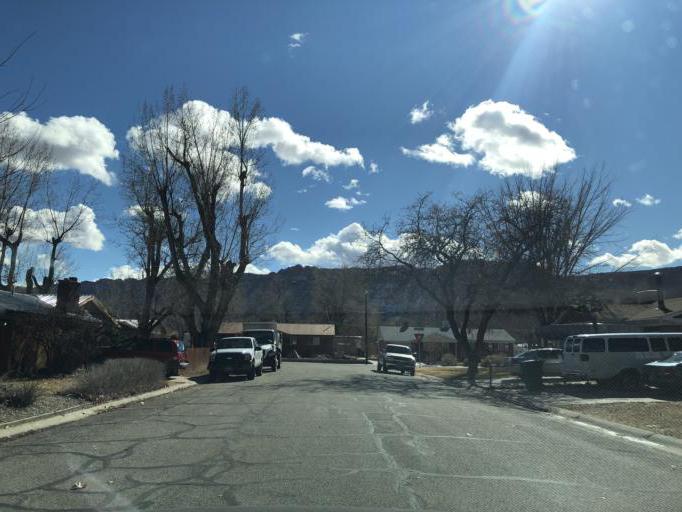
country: US
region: Utah
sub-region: Grand County
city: Moab
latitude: 38.5779
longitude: -109.5558
